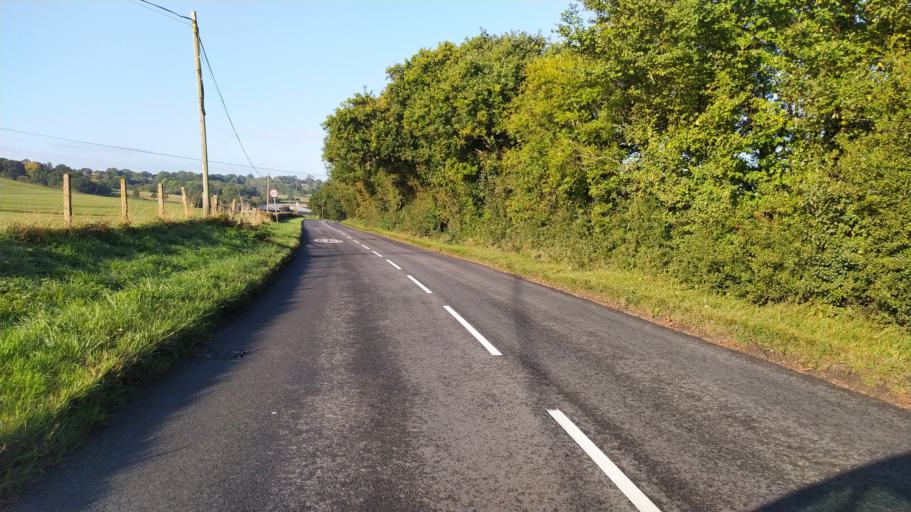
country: GB
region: England
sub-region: Dorset
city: Three Legged Cross
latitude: 50.8671
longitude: -1.9494
